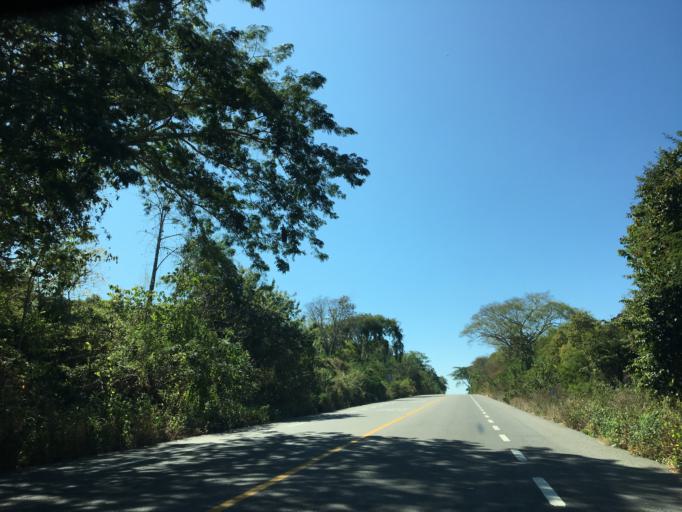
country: MX
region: Oaxaca
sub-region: Santa Maria Huatulco
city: Cuapinolito (Azulillo)
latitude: 15.7718
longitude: -96.2483
